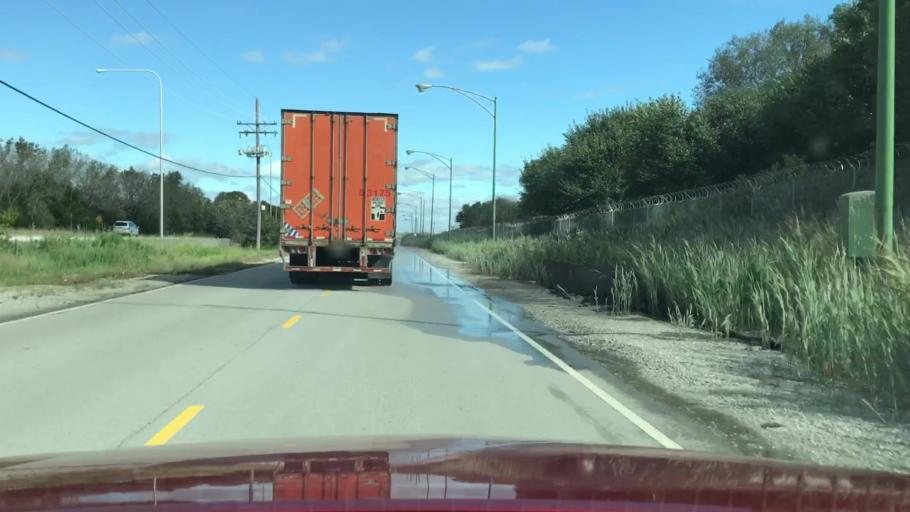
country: US
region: Illinois
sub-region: Cook County
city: Dolton
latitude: 41.7020
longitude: -87.5913
